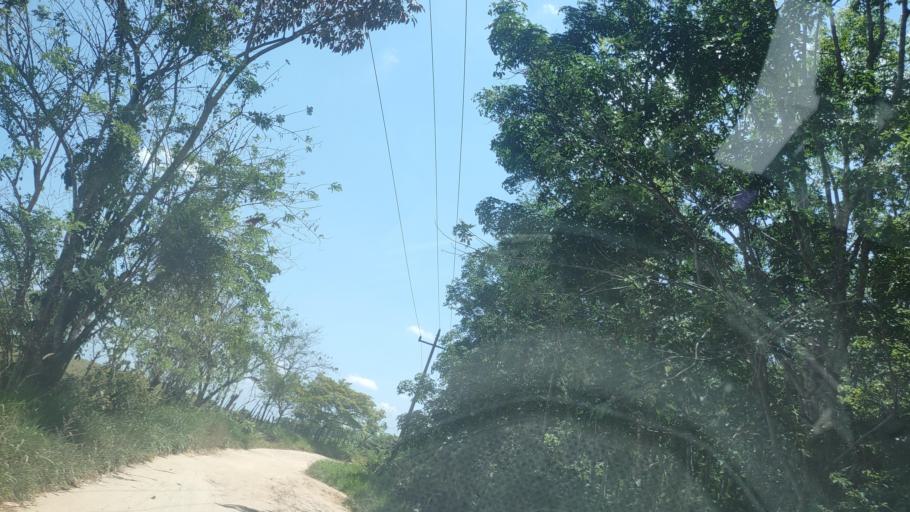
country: MX
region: Veracruz
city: Las Choapas
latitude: 17.7871
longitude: -94.1587
